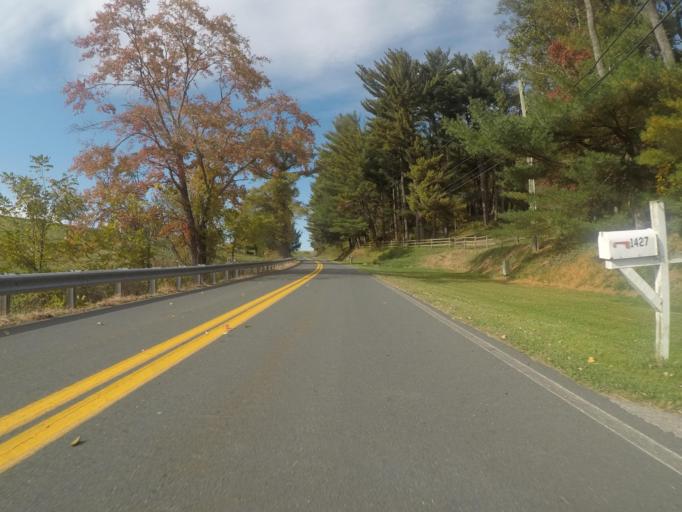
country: US
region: Maryland
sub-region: Carroll County
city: Hampstead
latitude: 39.5350
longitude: -76.8648
